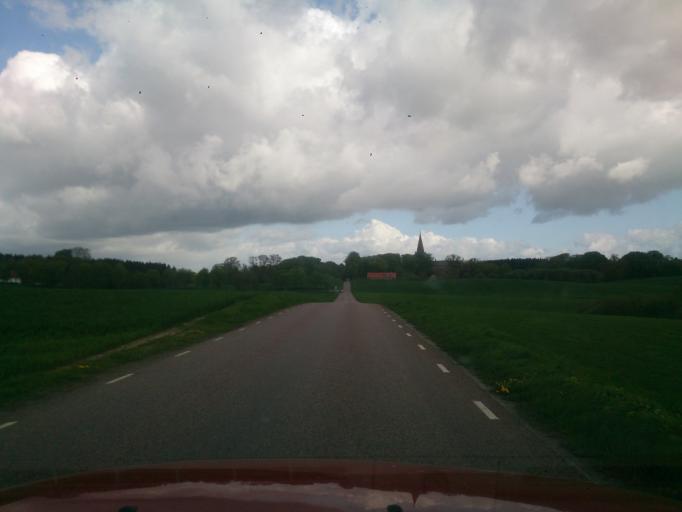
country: SE
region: Skane
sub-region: Ystads Kommun
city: Ystad
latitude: 55.4507
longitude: 13.7138
